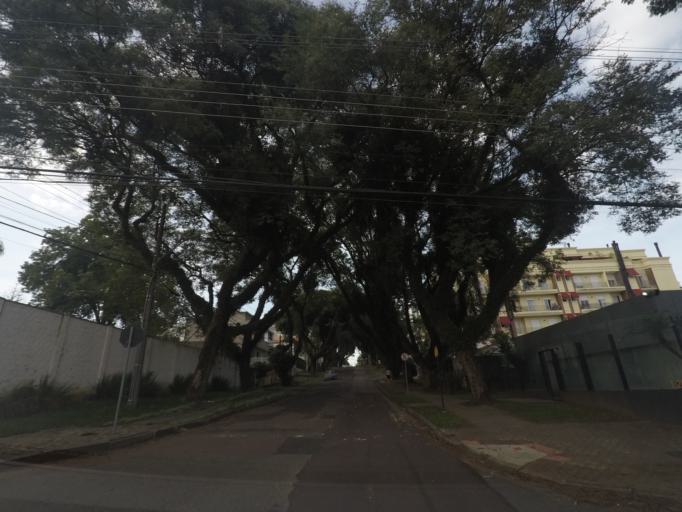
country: BR
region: Parana
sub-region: Curitiba
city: Curitiba
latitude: -25.4268
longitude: -49.2963
